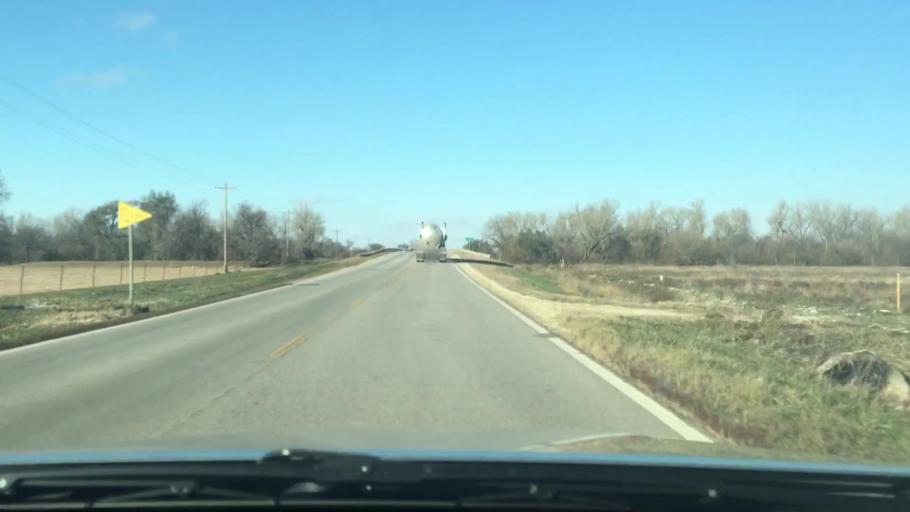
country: US
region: Kansas
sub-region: Rice County
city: Sterling
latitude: 38.1677
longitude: -98.2067
